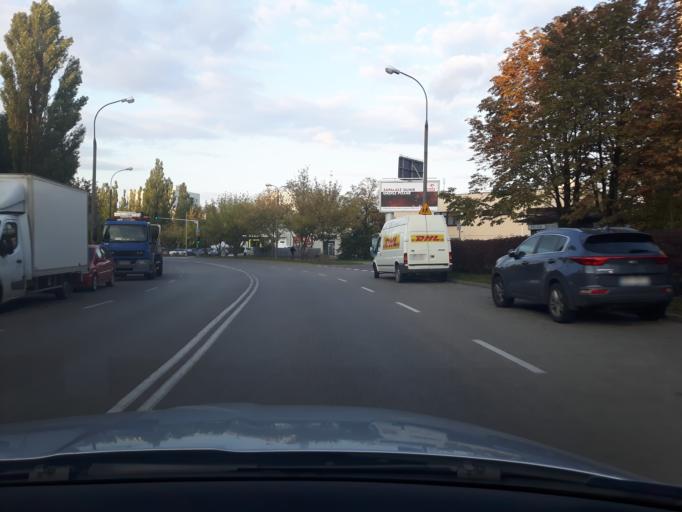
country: PL
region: Masovian Voivodeship
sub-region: Warszawa
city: Ursynow
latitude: 52.1576
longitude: 21.0369
